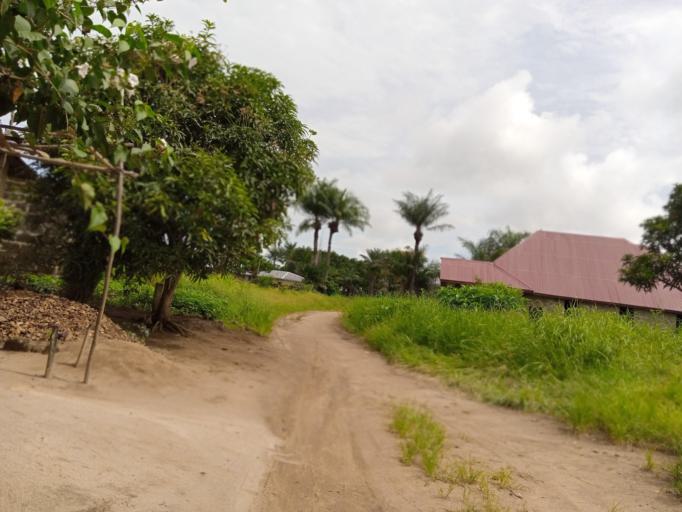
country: SL
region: Northern Province
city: Masoyila
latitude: 8.5911
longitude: -13.1953
